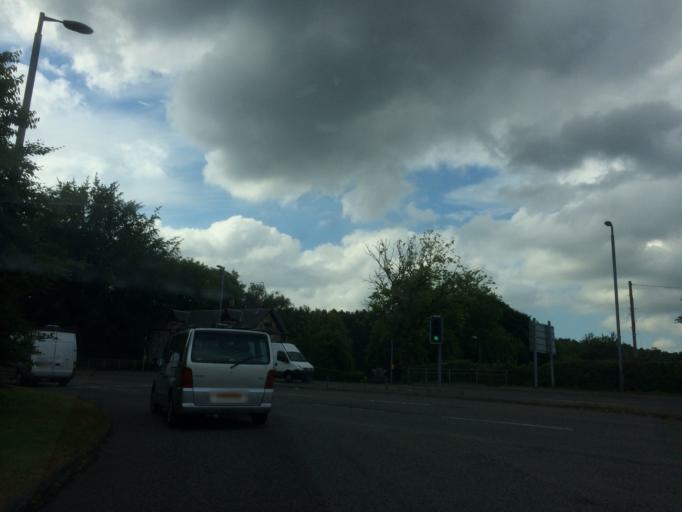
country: GB
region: Scotland
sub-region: East Renfrewshire
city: Giffnock
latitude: 55.8391
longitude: -4.3080
